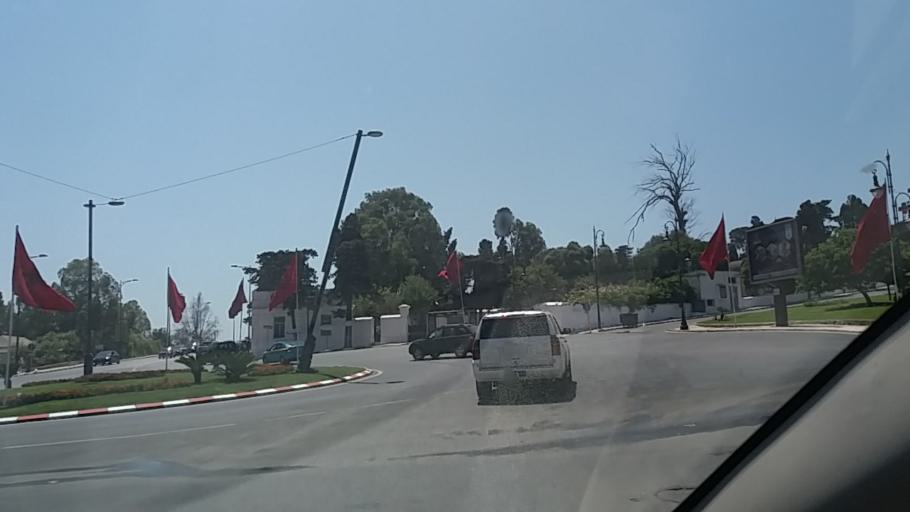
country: MA
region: Tanger-Tetouan
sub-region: Tanger-Assilah
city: Tangier
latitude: 35.7813
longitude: -5.8424
